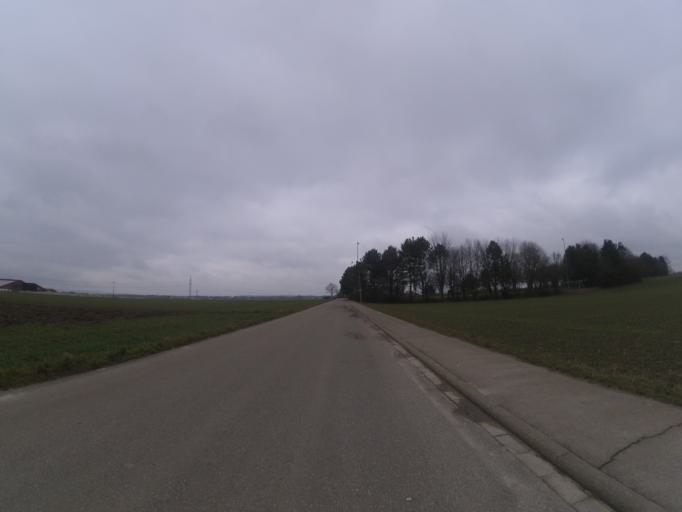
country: DE
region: Baden-Wuerttemberg
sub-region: Tuebingen Region
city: Dornstadt
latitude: 48.4381
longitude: 9.9675
